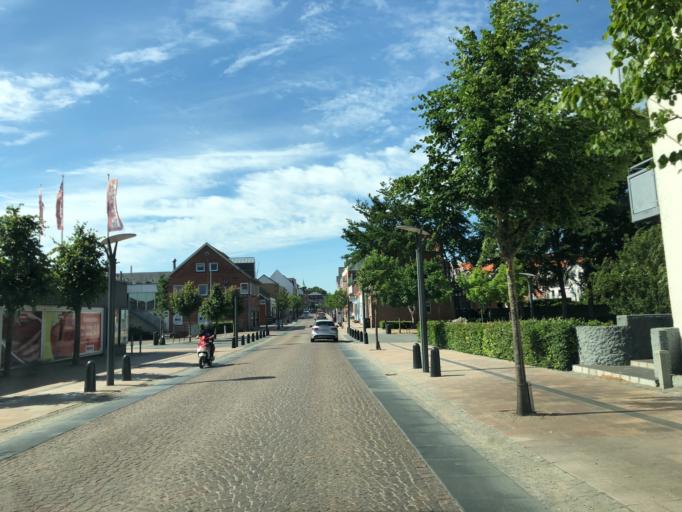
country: DK
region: Central Jutland
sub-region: Ikast-Brande Kommune
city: Brande
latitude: 55.9415
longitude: 9.1301
